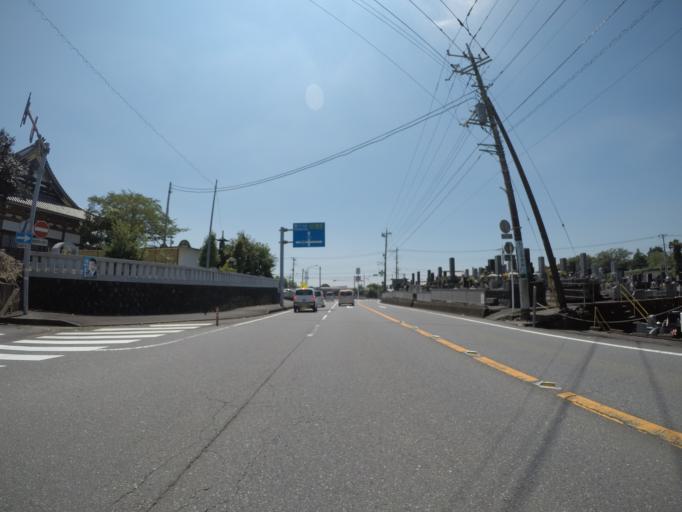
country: JP
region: Shizuoka
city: Fuji
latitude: 35.1960
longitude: 138.6810
